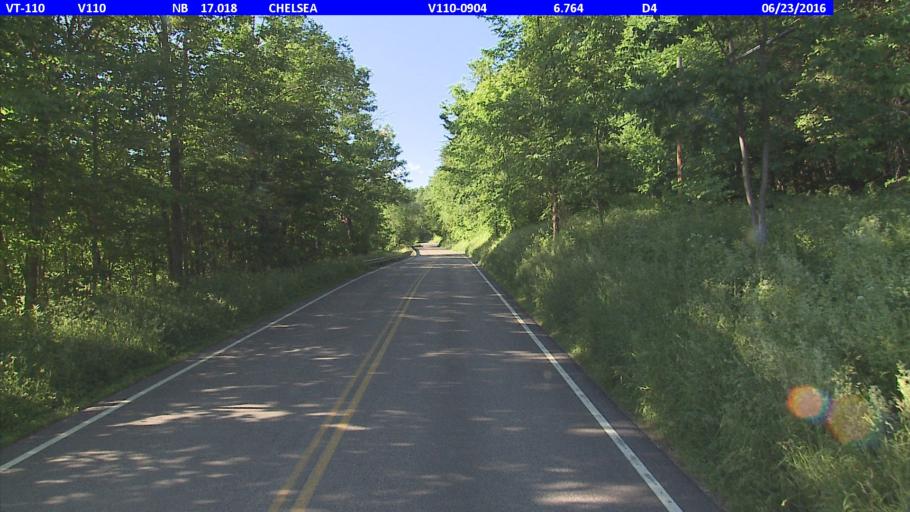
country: US
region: Vermont
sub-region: Orange County
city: Chelsea
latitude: 44.0379
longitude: -72.4743
